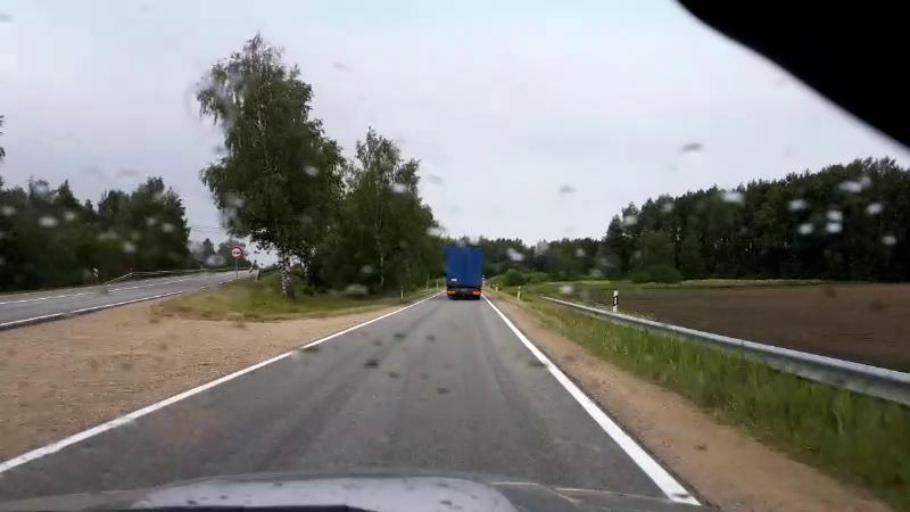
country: LV
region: Salaspils
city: Salaspils
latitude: 56.8475
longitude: 24.3964
